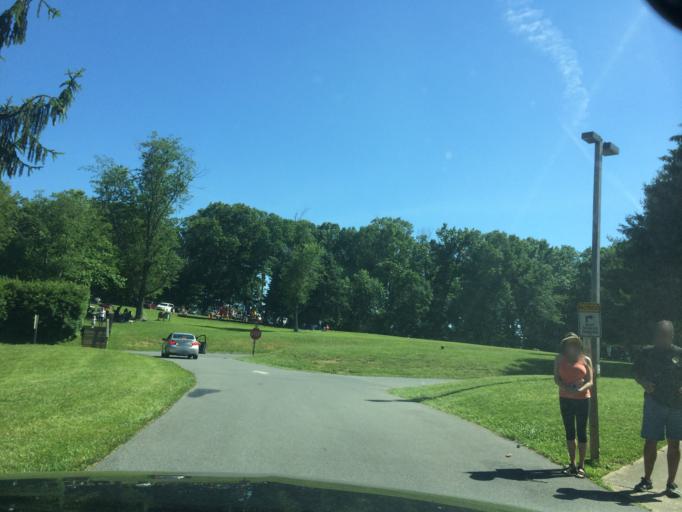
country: US
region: Maryland
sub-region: Carroll County
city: Sykesville
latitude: 39.3979
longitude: -76.9873
